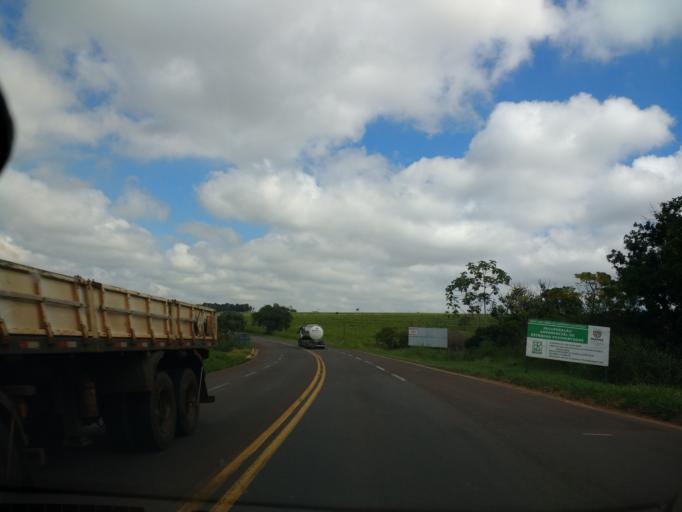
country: BR
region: Parana
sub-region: Cruzeiro Do Oeste
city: Cruzeiro do Oeste
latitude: -23.7741
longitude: -53.0223
